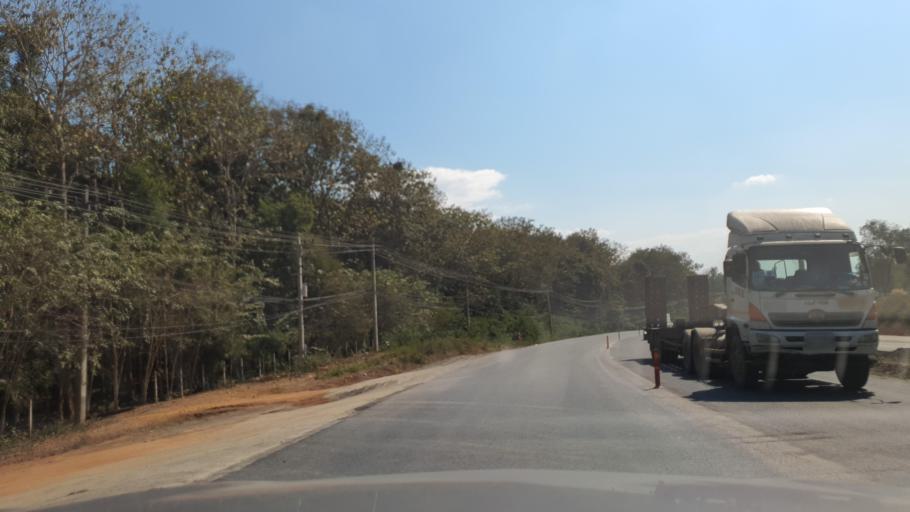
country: TH
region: Nan
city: Nan
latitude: 18.8255
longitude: 100.7656
